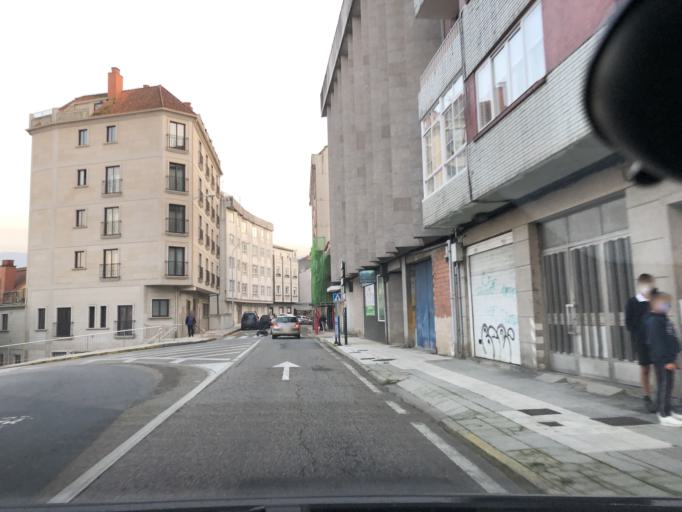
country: ES
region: Galicia
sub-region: Provincia de Pontevedra
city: Marin
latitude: 42.3933
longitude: -8.7065
